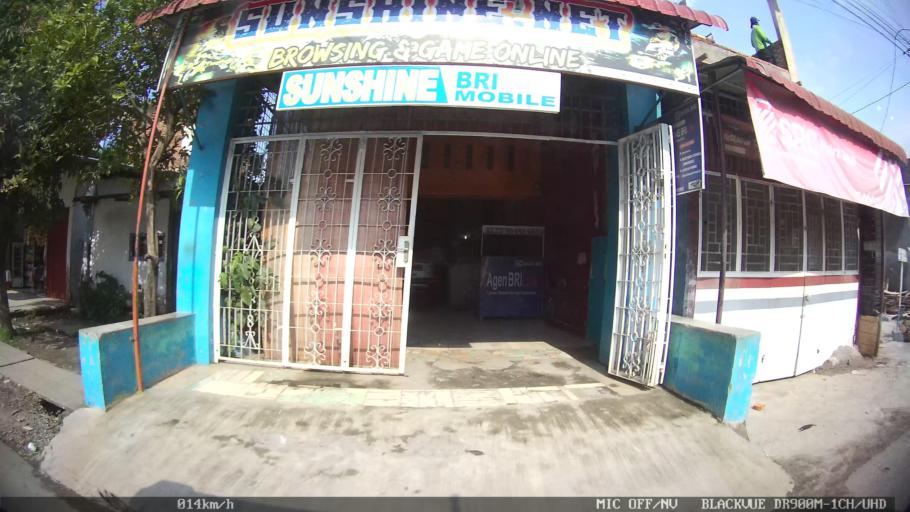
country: ID
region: North Sumatra
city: Medan
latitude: 3.5813
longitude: 98.7567
